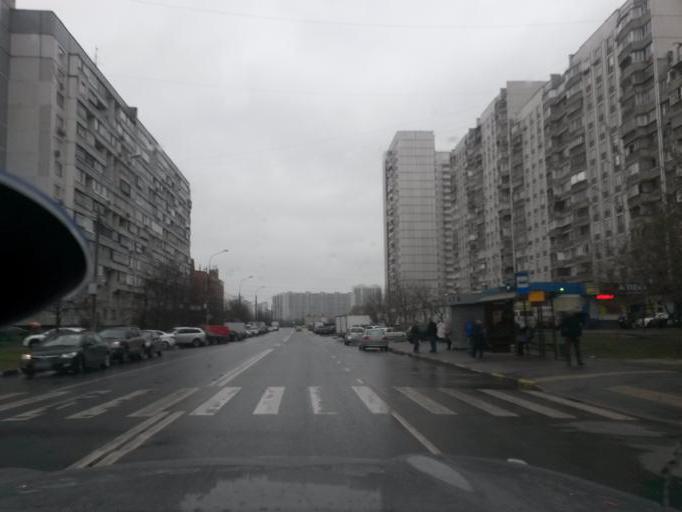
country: RU
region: Moscow
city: Brateyevo
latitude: 55.6472
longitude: 37.7530
